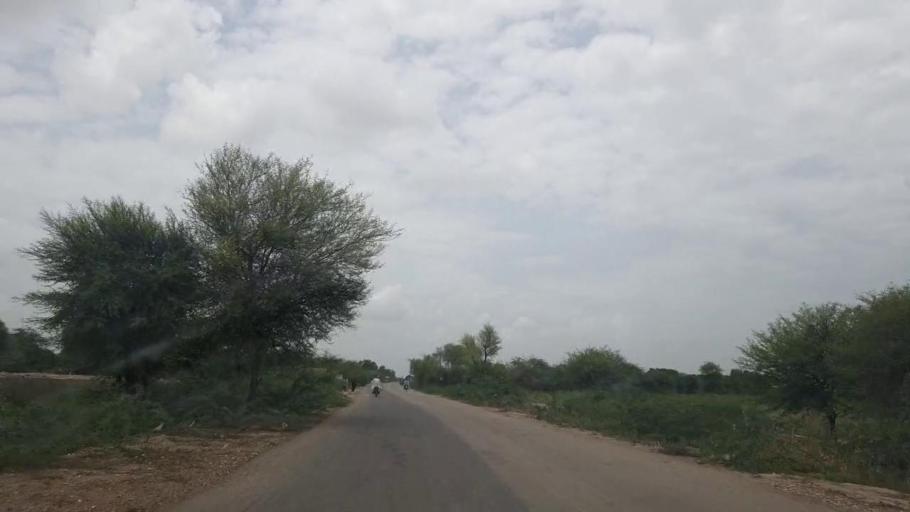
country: PK
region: Sindh
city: Naukot
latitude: 24.8898
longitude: 69.2526
